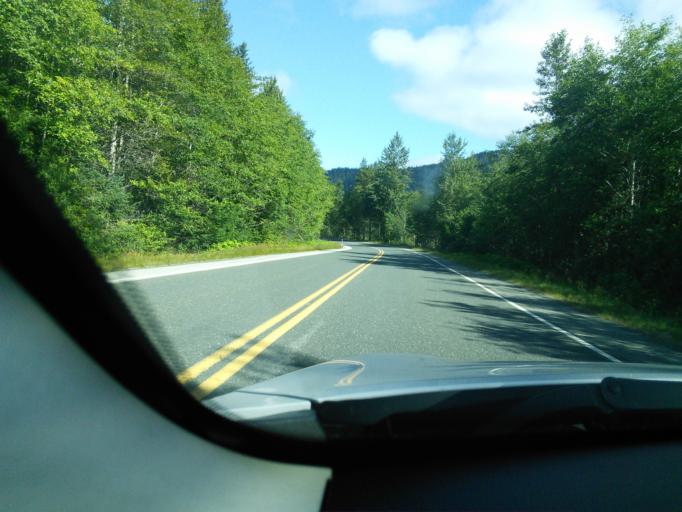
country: CA
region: British Columbia
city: Campbell River
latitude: 50.3583
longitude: -125.9131
